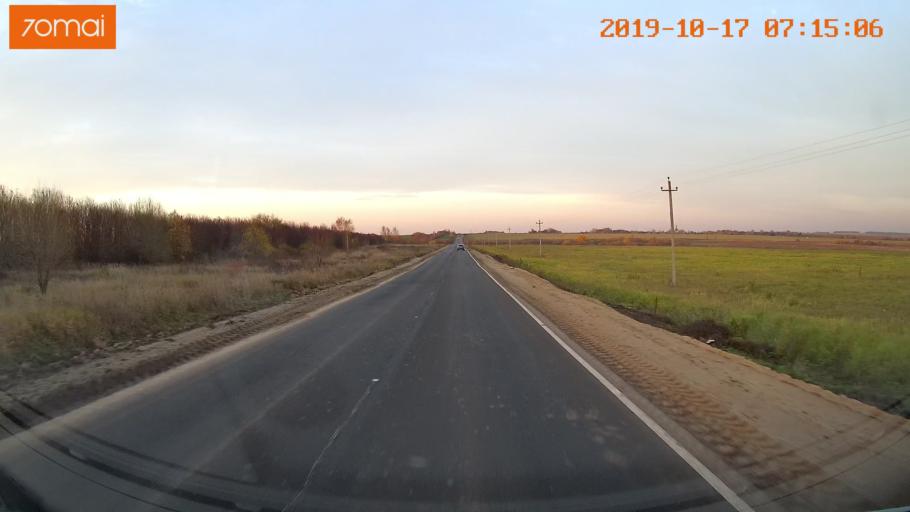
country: RU
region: Vladimir
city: Suzdal'
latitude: 56.3841
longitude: 40.2746
